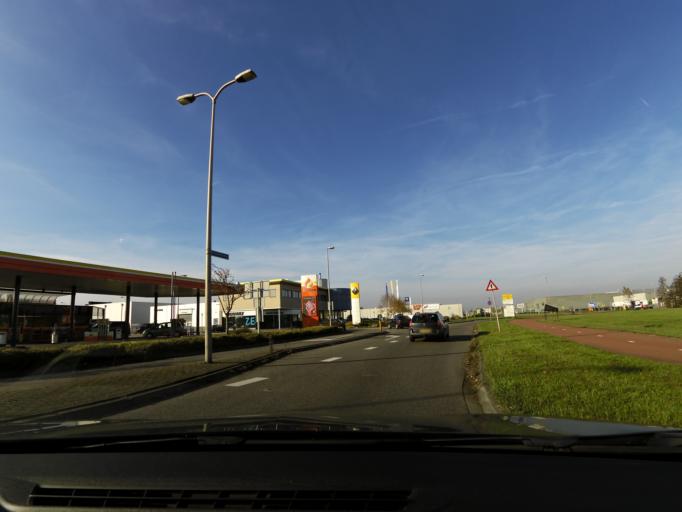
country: NL
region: South Holland
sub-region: Gemeente Zwijndrecht
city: Heerjansdam
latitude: 51.8550
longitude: 4.5627
